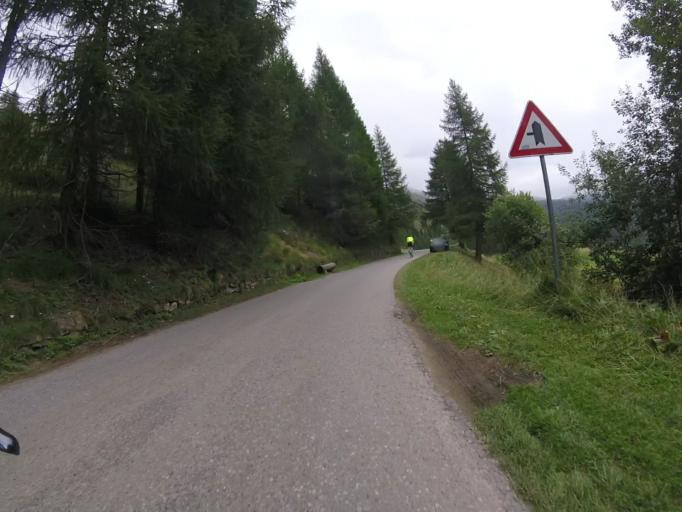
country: IT
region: Lombardy
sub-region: Provincia di Brescia
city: Monno
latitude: 46.2490
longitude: 10.3066
